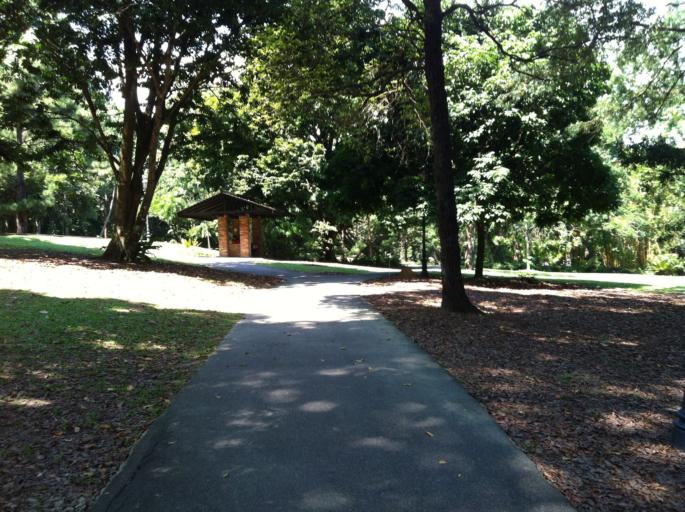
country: SG
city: Singapore
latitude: 1.3078
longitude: 103.8167
